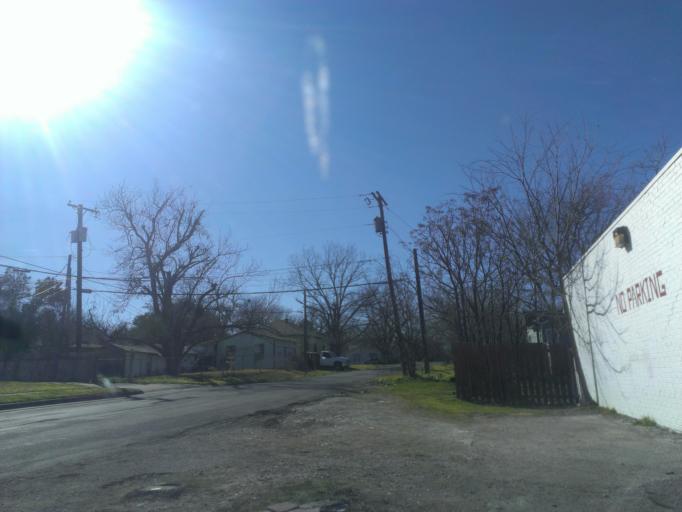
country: US
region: Texas
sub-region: Williamson County
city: Taylor
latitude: 30.5772
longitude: -97.4107
